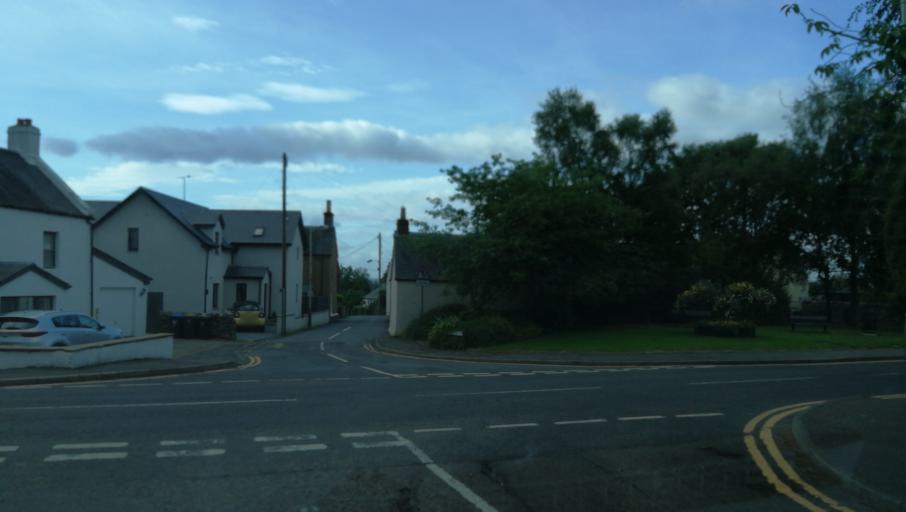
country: GB
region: Scotland
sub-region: Perth and Kinross
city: Blairgowrie
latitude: 56.5966
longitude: -3.3218
